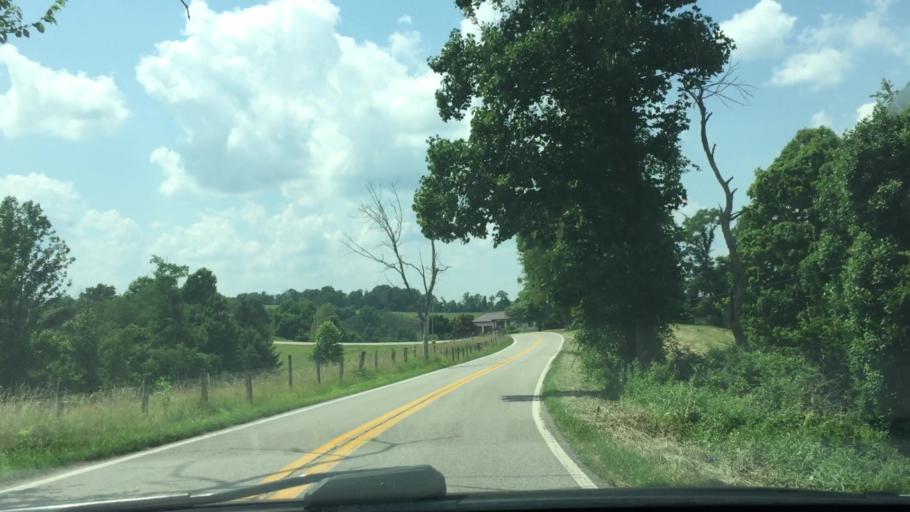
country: US
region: West Virginia
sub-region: Wetzel County
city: New Martinsville
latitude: 39.7017
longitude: -80.7475
